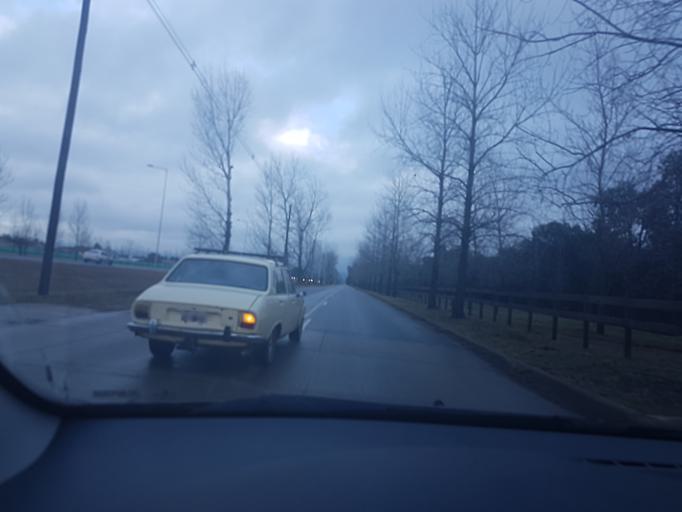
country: AR
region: Cordoba
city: Villa Allende
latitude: -31.3029
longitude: -64.2373
